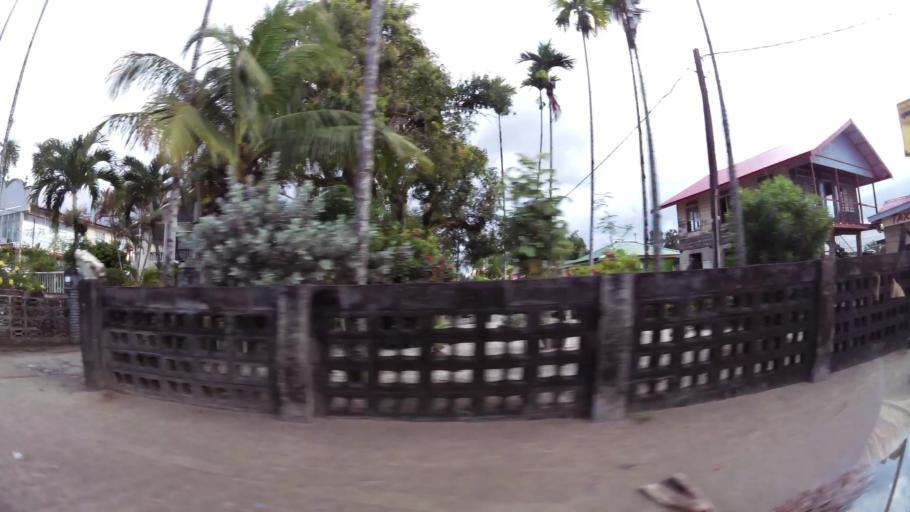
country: SR
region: Paramaribo
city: Paramaribo
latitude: 5.8463
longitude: -55.2298
